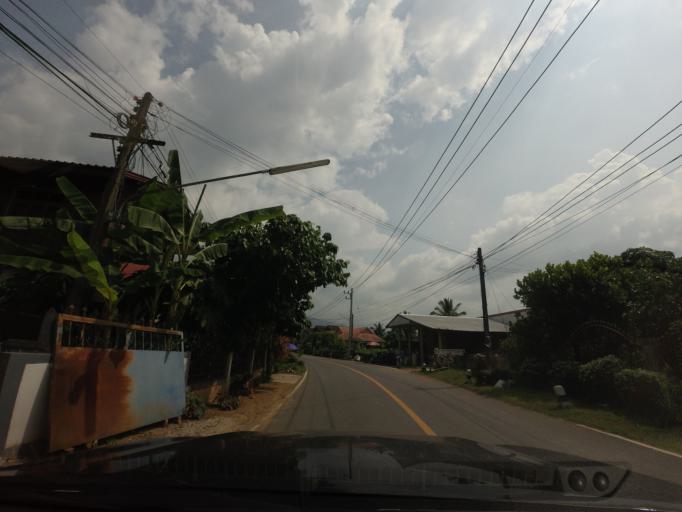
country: TH
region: Nan
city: Pua
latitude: 19.1803
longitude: 100.9443
